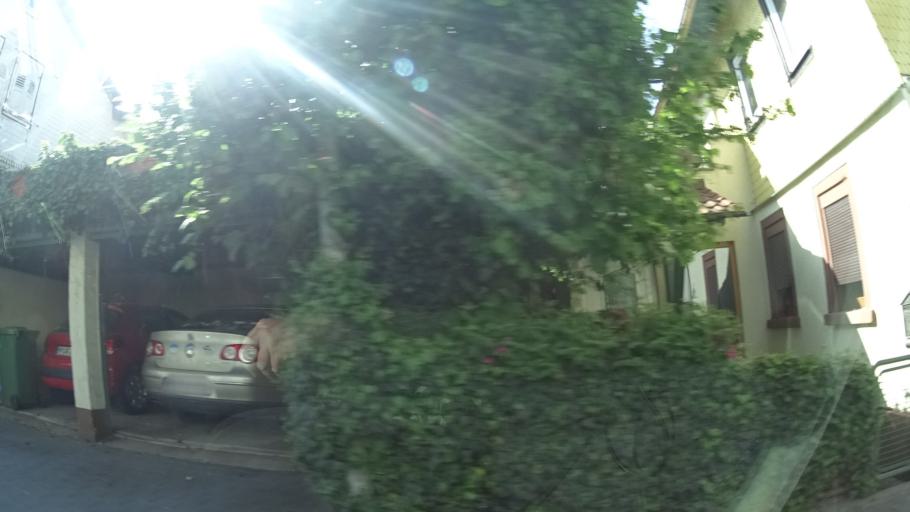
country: DE
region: Hesse
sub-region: Regierungsbezirk Darmstadt
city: Furth
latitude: 49.6374
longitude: 8.8335
